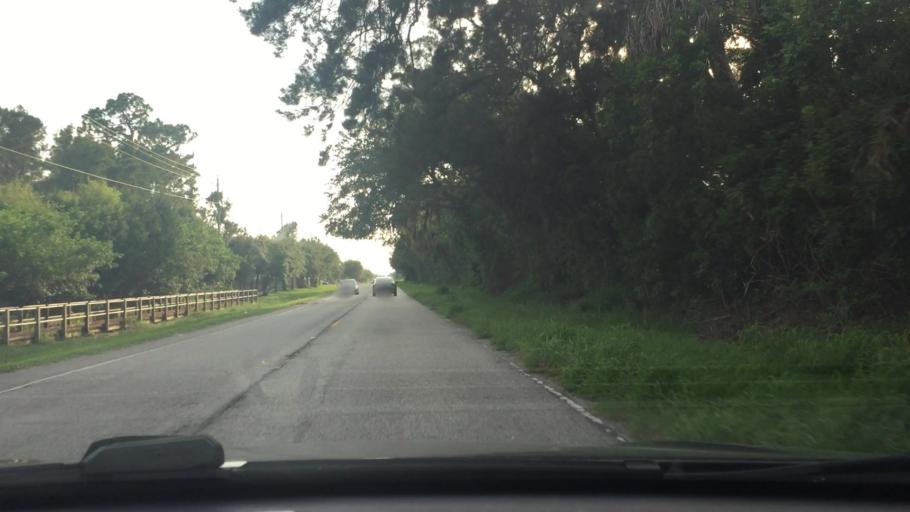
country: US
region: Florida
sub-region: Hillsborough County
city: Ruskin
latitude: 27.6948
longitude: -82.4283
